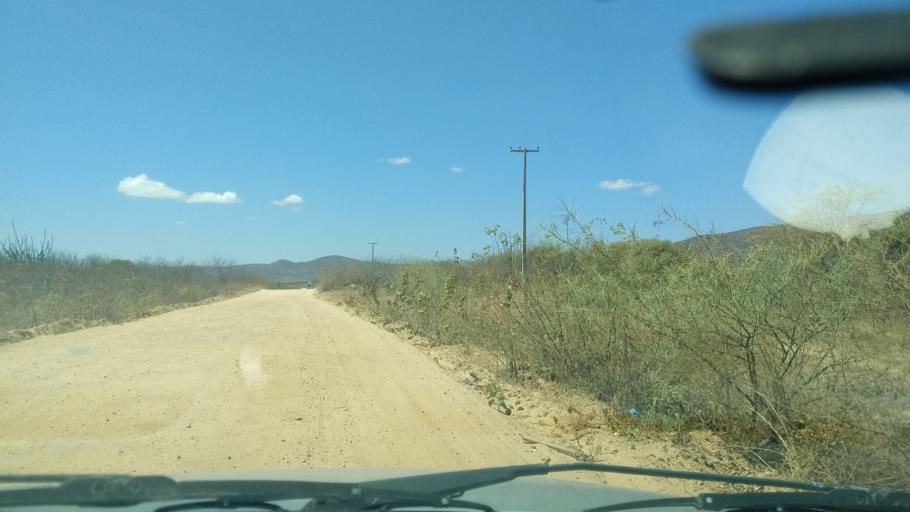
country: BR
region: Rio Grande do Norte
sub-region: Sao Tome
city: Sao Tome
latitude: -5.9732
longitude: -36.1658
